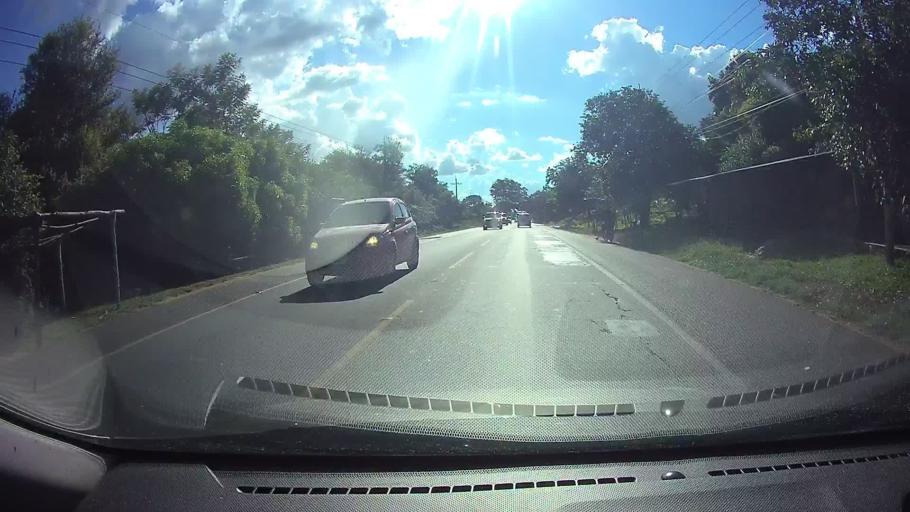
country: PY
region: Cordillera
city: Caacupe
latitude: -25.3883
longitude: -57.1040
